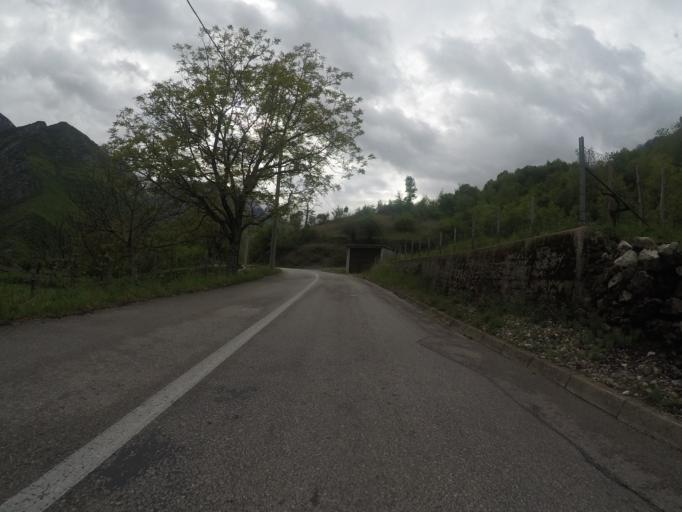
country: BA
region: Federation of Bosnia and Herzegovina
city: Siroki Brijeg
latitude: 43.5393
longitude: 17.5974
